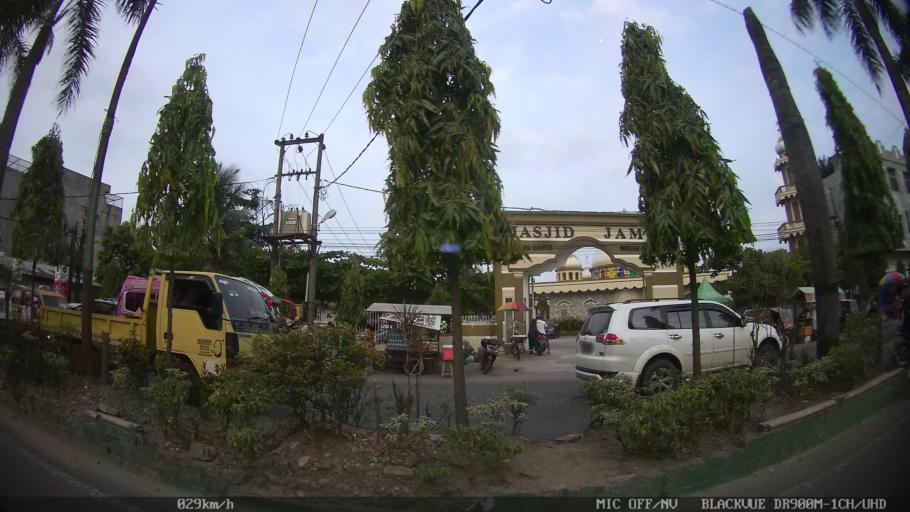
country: ID
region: North Sumatra
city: Sunggal
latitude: 3.5965
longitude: 98.6091
